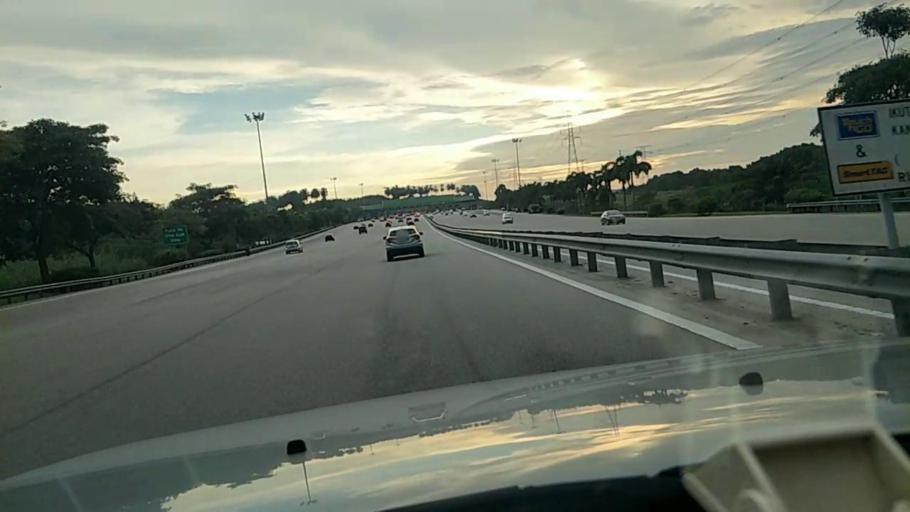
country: MY
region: Selangor
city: Shah Alam
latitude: 3.0919
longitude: 101.4915
